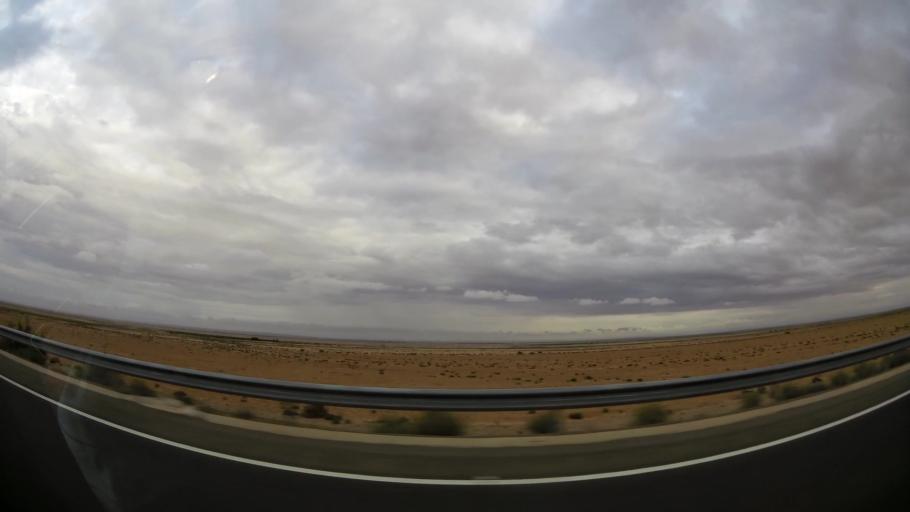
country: MA
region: Taza-Al Hoceima-Taounate
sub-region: Taza
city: Guercif
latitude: 34.3263
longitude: -3.5585
